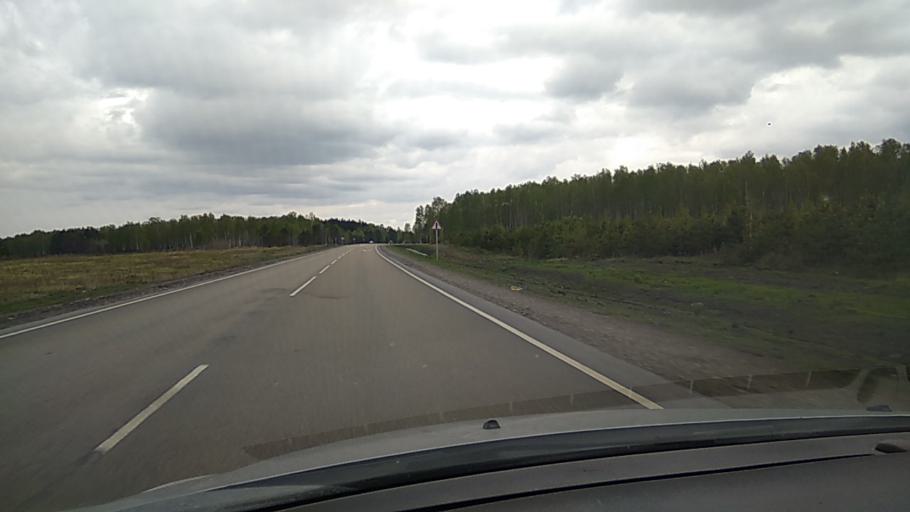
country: RU
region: Kurgan
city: Kataysk
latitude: 56.2965
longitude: 62.3990
